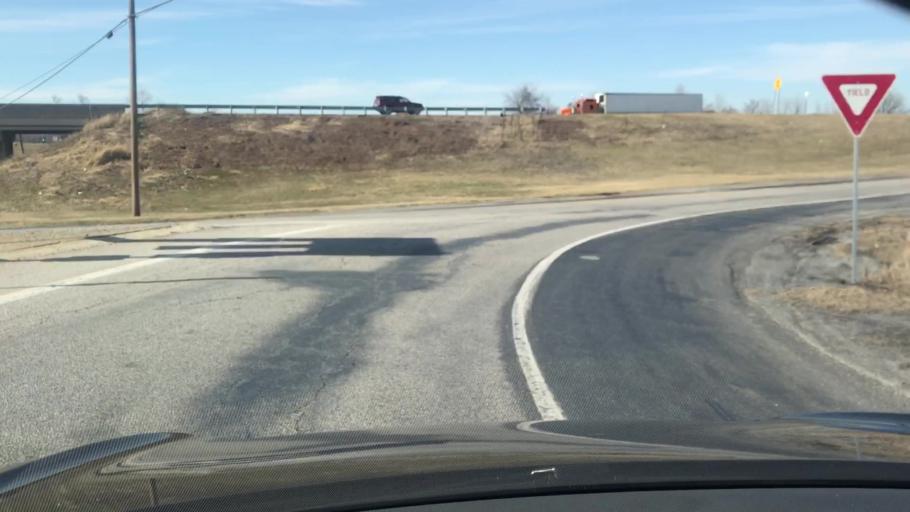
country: US
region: Pennsylvania
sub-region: Cumberland County
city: Newville
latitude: 40.1283
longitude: -77.3494
